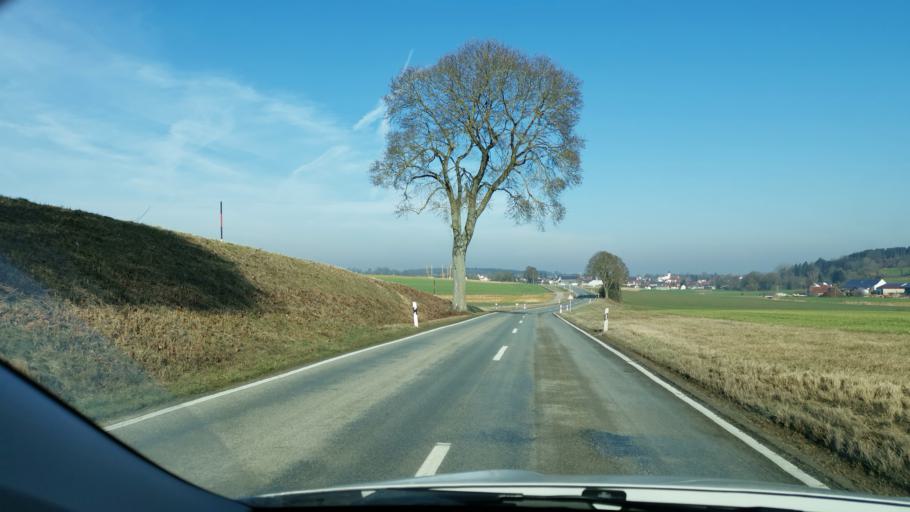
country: DE
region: Bavaria
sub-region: Swabia
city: Holzheim
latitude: 48.5991
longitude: 10.9510
